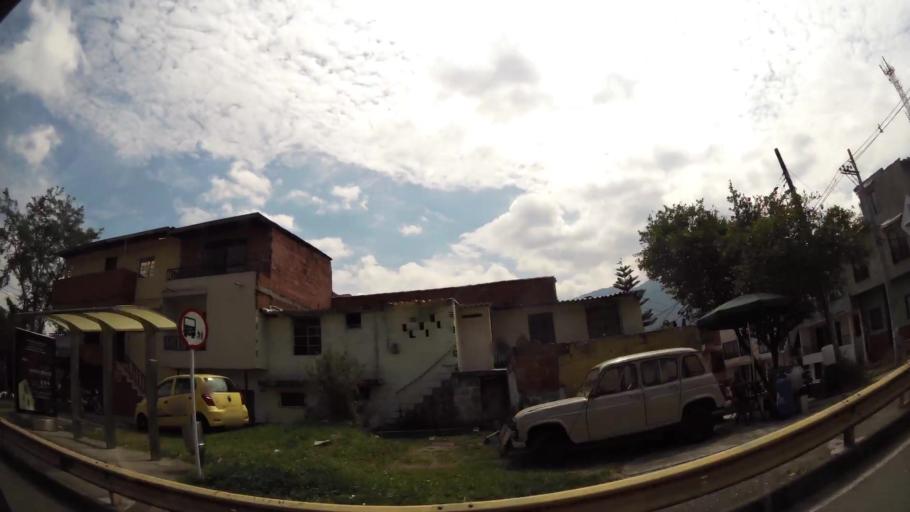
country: CO
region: Antioquia
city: Bello
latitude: 6.3110
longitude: -75.5638
